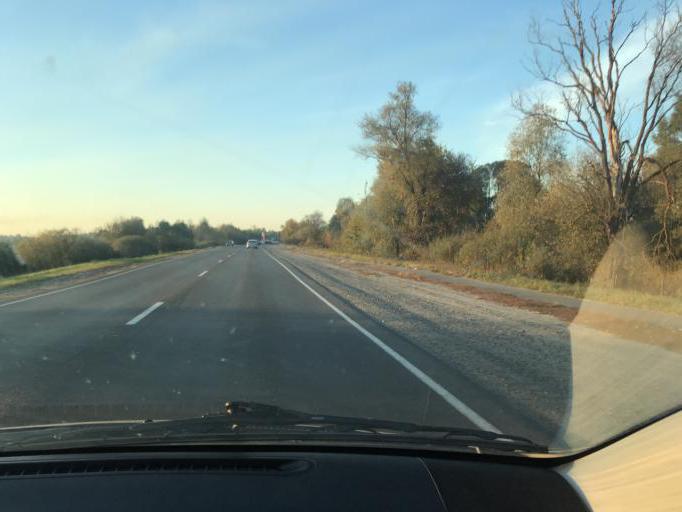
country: BY
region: Brest
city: Pinsk
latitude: 52.0988
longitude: 26.1170
